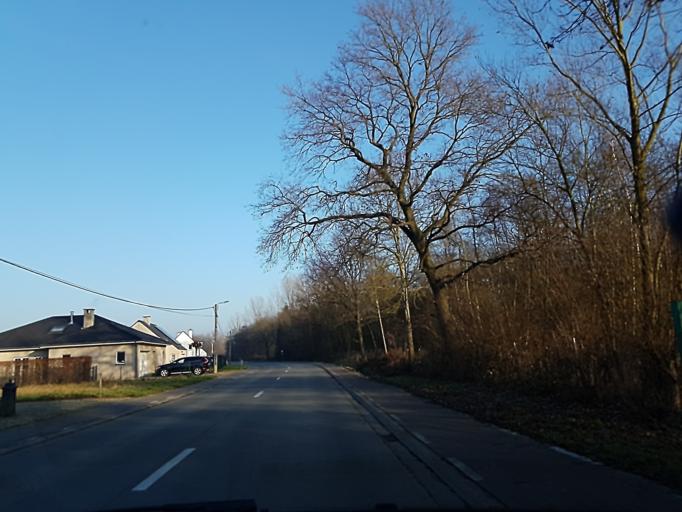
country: BE
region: Flanders
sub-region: Provincie Vlaams-Brabant
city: Tremelo
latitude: 51.0176
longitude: 4.7378
